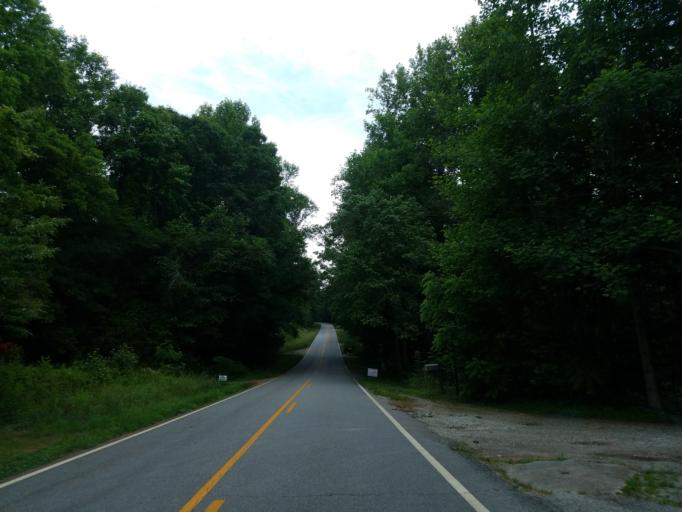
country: US
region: Georgia
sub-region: Lumpkin County
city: Dahlonega
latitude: 34.6106
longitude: -83.9733
